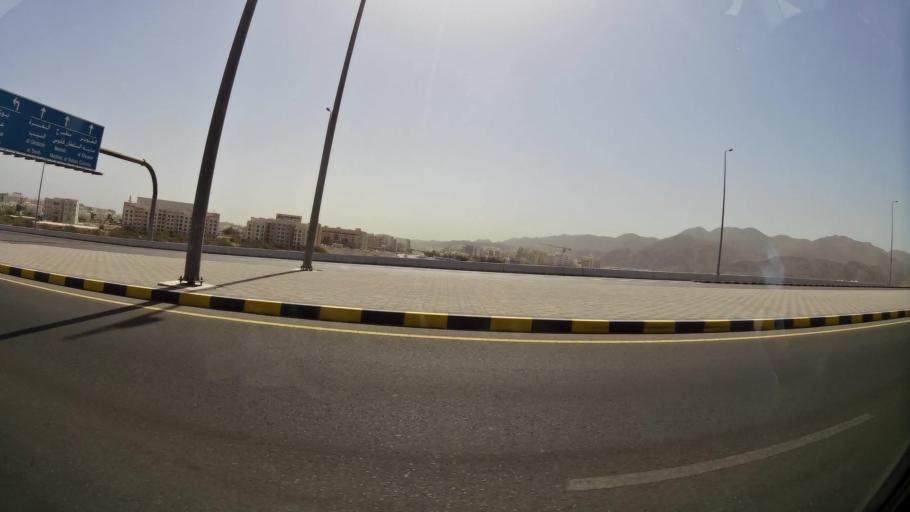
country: OM
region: Muhafazat Masqat
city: Bawshar
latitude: 23.5840
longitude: 58.4160
